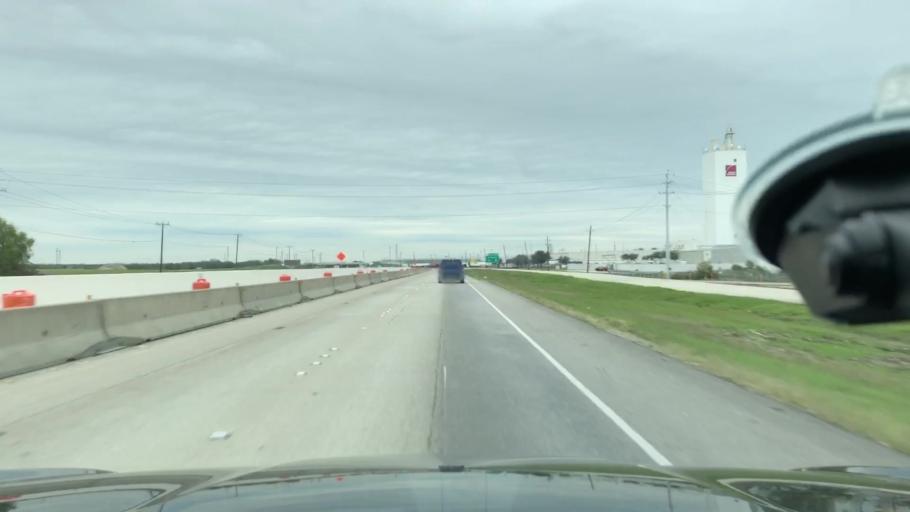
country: US
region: Texas
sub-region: Ellis County
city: Waxahachie
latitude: 32.4378
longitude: -96.8534
